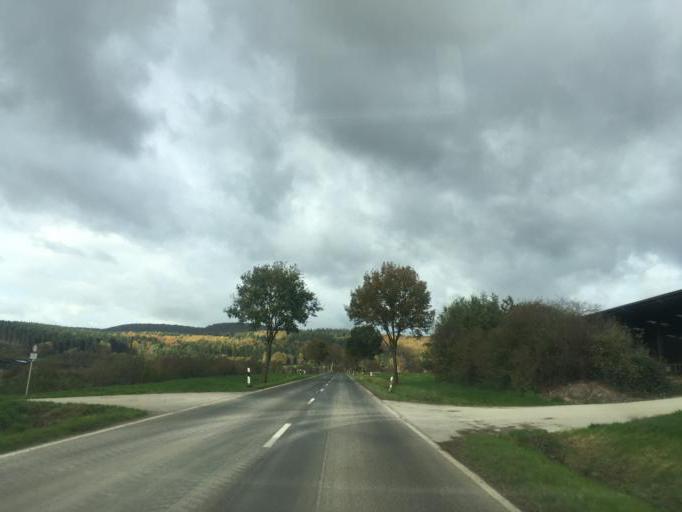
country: DE
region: Lower Saxony
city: Bodenfelde
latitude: 51.6400
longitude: 9.5208
